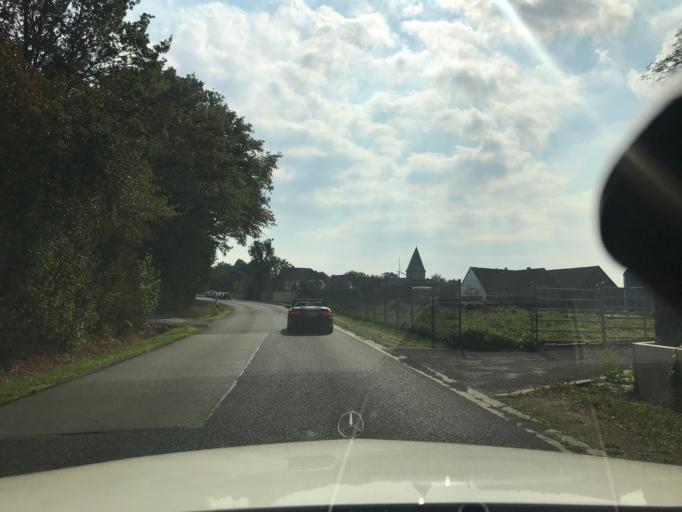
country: DE
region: North Rhine-Westphalia
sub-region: Regierungsbezirk Arnsberg
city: Werl
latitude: 51.5796
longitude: 7.8670
